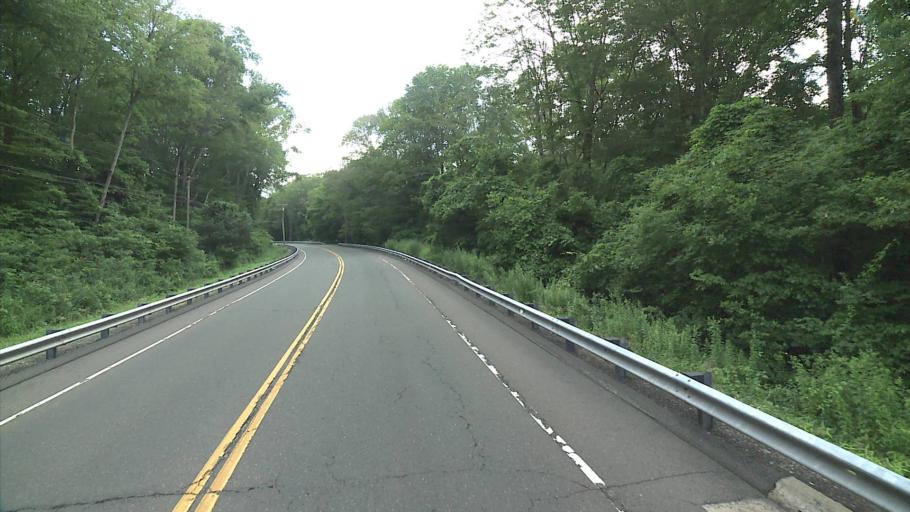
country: US
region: Connecticut
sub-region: Middlesex County
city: Deep River Center
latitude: 41.3504
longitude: -72.4964
